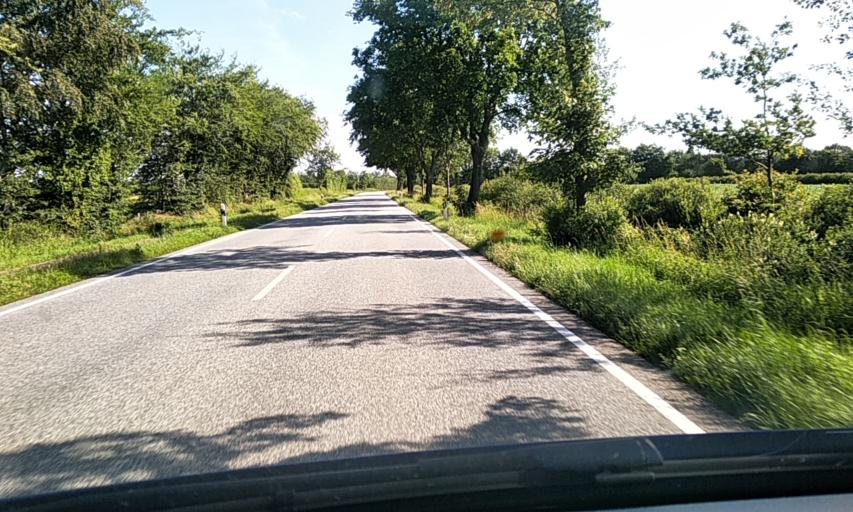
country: DE
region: Schleswig-Holstein
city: Fockbek
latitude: 54.2893
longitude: 9.5812
